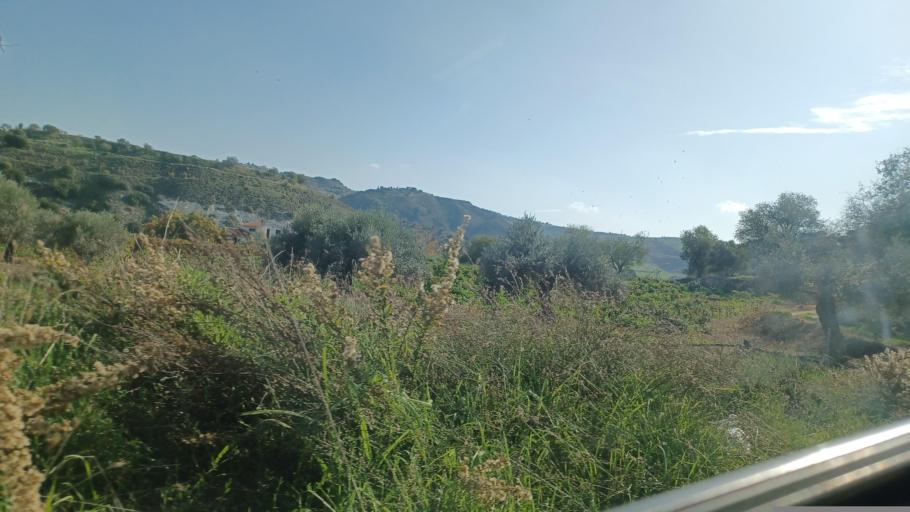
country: CY
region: Pafos
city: Mesogi
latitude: 34.7677
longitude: 32.5742
